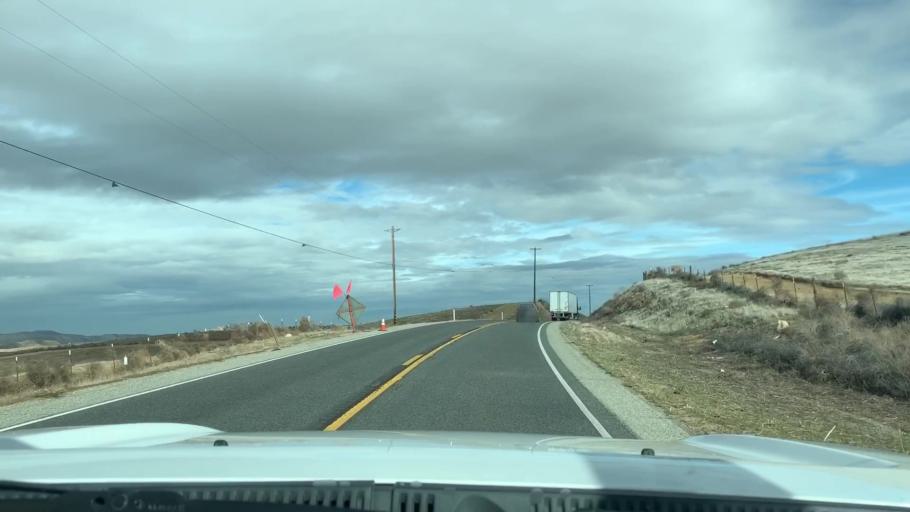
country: US
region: California
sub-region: Kern County
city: Maricopa
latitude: 34.9580
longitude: -119.4493
